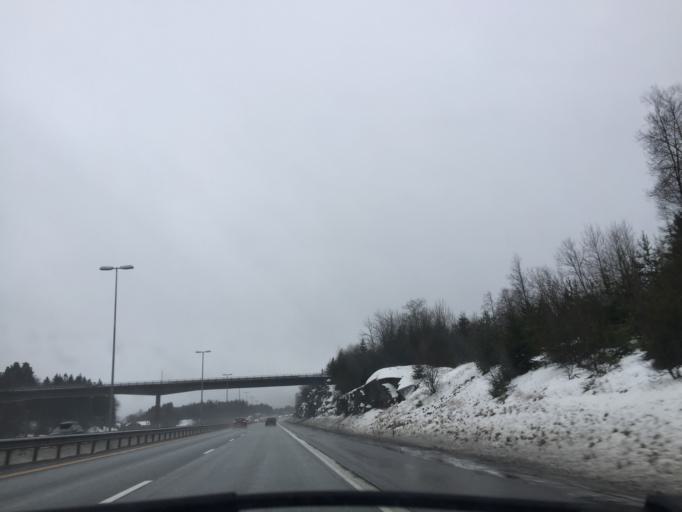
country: NO
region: Akershus
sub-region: Vestby
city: Vestby
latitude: 59.5850
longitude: 10.7338
